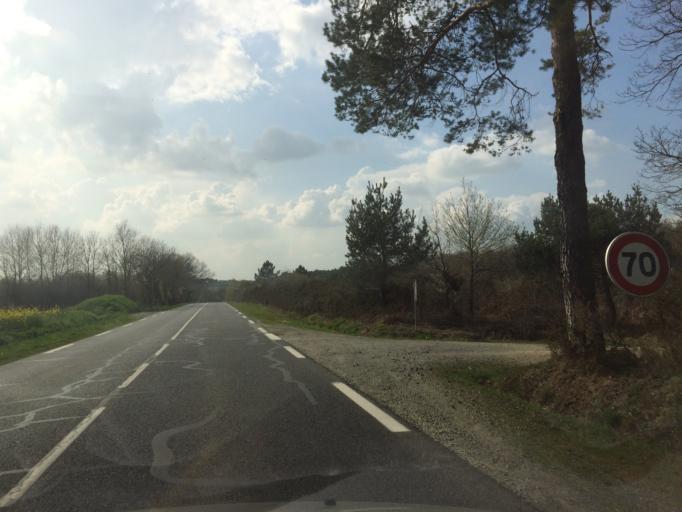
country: FR
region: Pays de la Loire
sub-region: Departement de la Loire-Atlantique
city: Bouvron
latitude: 47.4854
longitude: -1.8431
